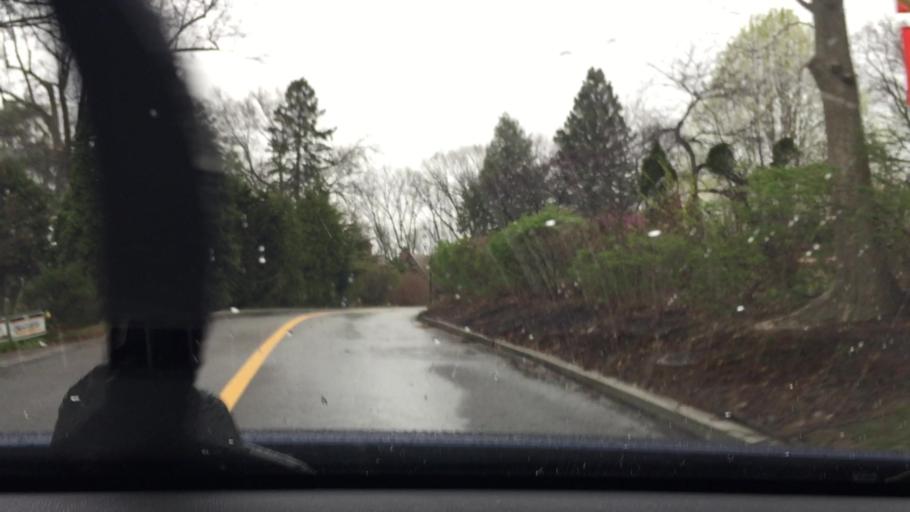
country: US
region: Pennsylvania
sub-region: Allegheny County
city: Ben Avon
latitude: 40.5134
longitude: -80.0765
